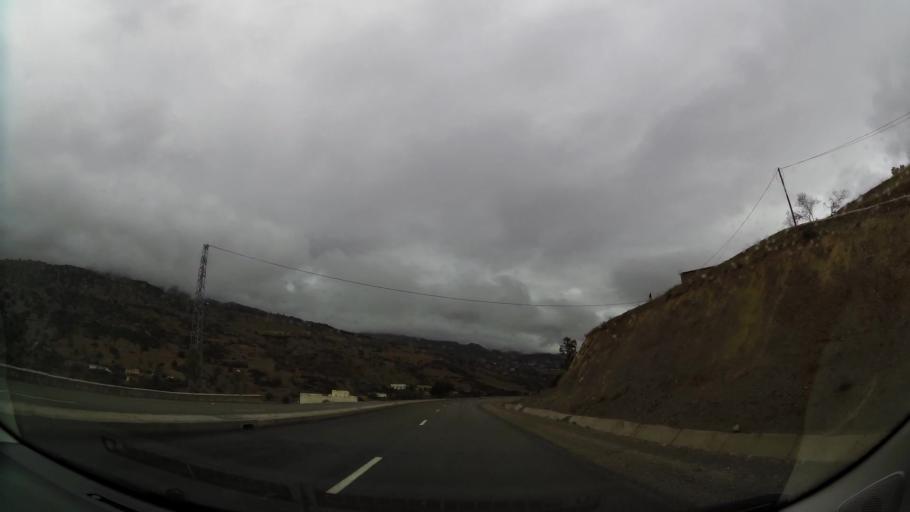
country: MA
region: Taza-Al Hoceima-Taounate
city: Imzourene
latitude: 34.9795
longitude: -3.8112
